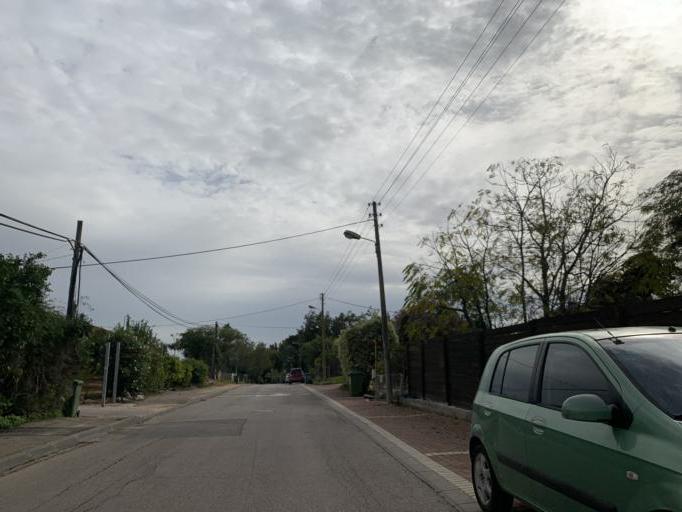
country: IL
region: Central District
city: Hod HaSharon
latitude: 32.1513
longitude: 34.8992
